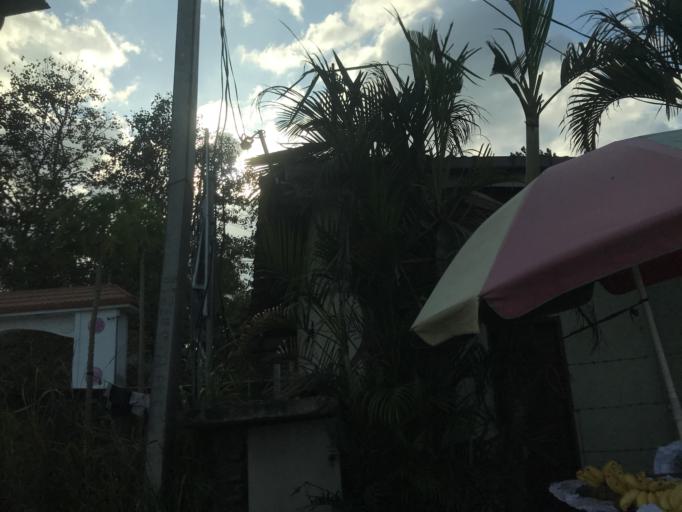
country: LK
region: Western
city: Gampaha
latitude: 7.1000
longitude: 79.9911
